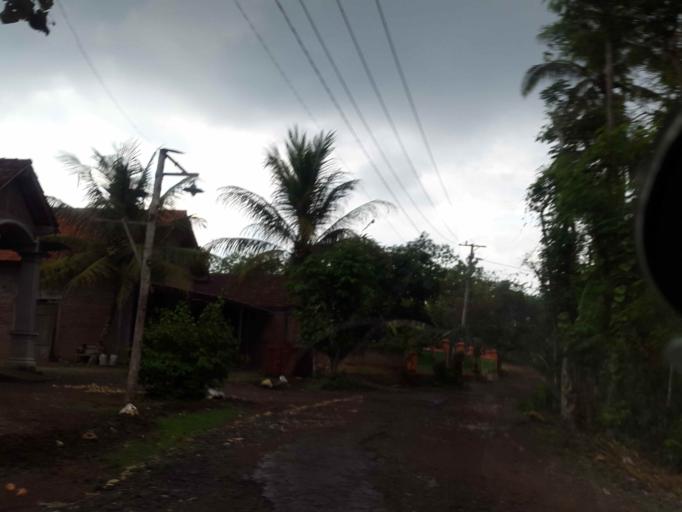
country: ID
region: East Java
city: Tumpakjoho
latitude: -8.2007
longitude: 111.9289
